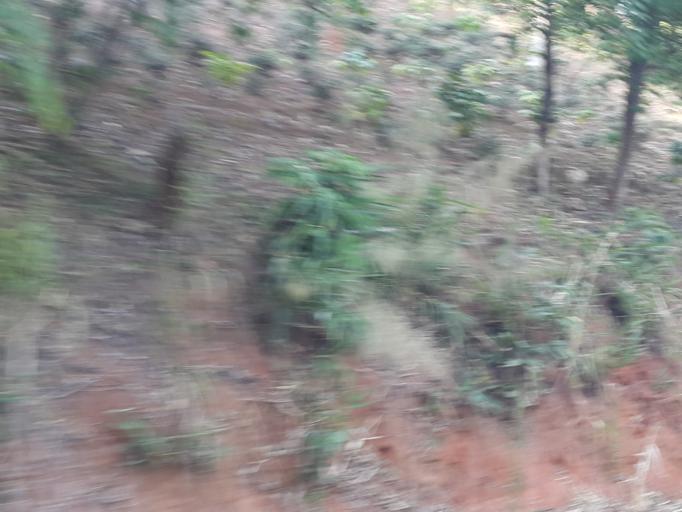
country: TH
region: Chiang Mai
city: Samoeng
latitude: 18.9099
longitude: 98.7967
